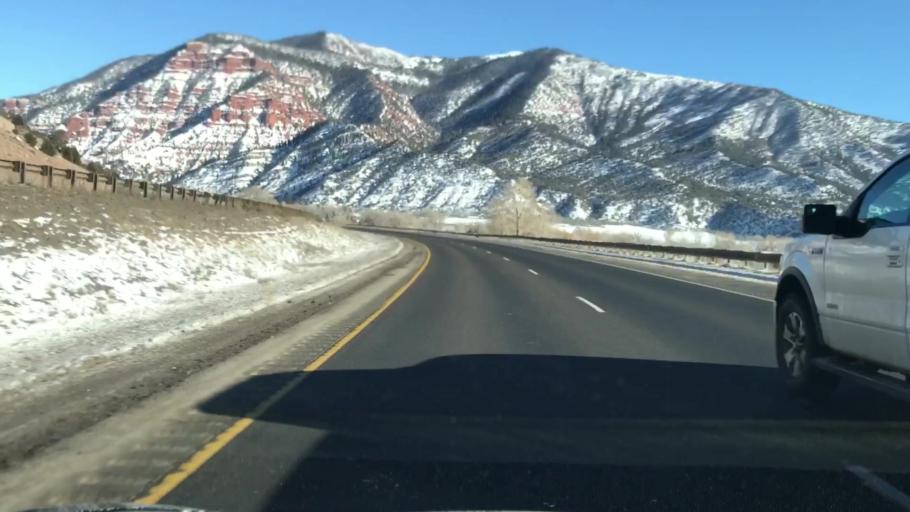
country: US
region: Colorado
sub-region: Eagle County
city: Eagle
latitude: 39.6800
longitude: -106.7690
